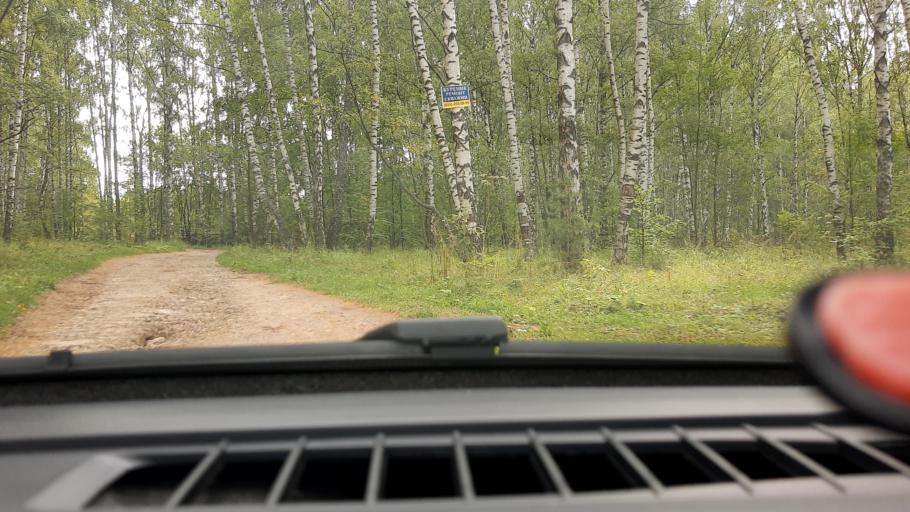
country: RU
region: Nizjnij Novgorod
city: Burevestnik
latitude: 56.0176
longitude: 43.7194
